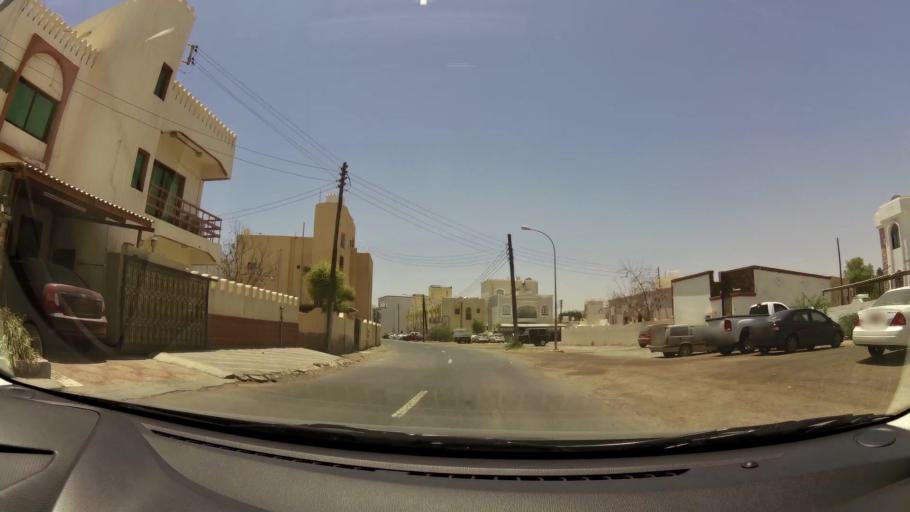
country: OM
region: Muhafazat Masqat
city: As Sib al Jadidah
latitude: 23.6322
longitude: 58.2426
